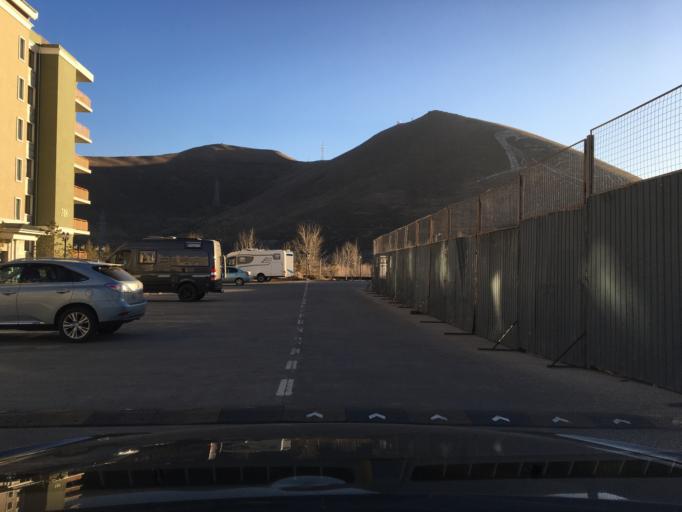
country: MN
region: Ulaanbaatar
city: Ulaanbaatar
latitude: 47.8895
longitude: 106.9286
